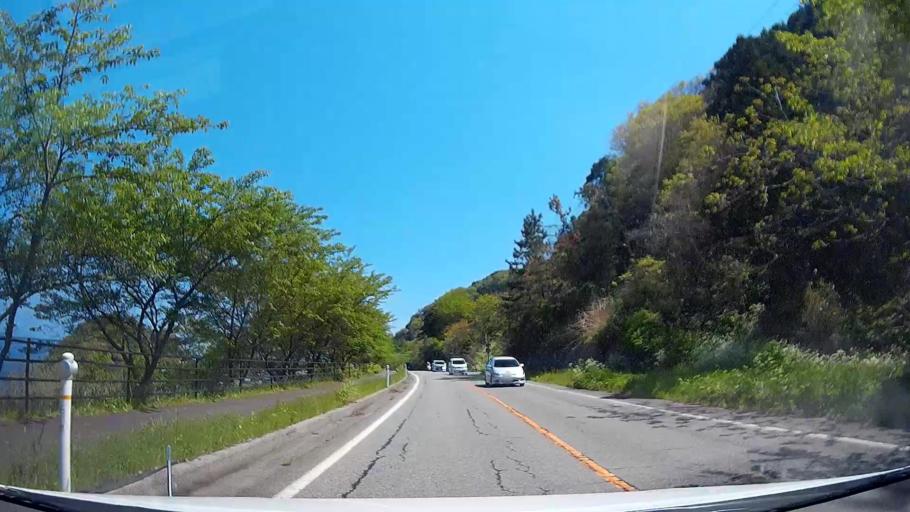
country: JP
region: Ishikawa
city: Nanao
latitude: 37.4131
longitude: 136.9769
